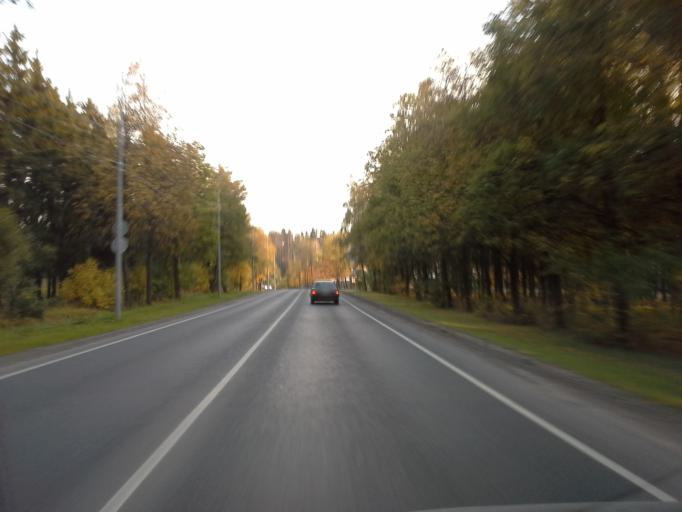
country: RU
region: Moskovskaya
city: Zhavoronki
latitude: 55.6633
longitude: 37.0932
